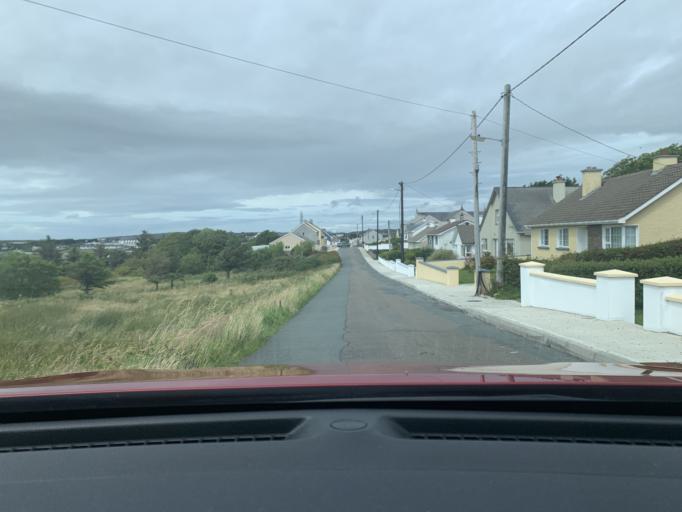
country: IE
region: Ulster
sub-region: County Donegal
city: Dungloe
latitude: 54.9458
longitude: -8.3589
